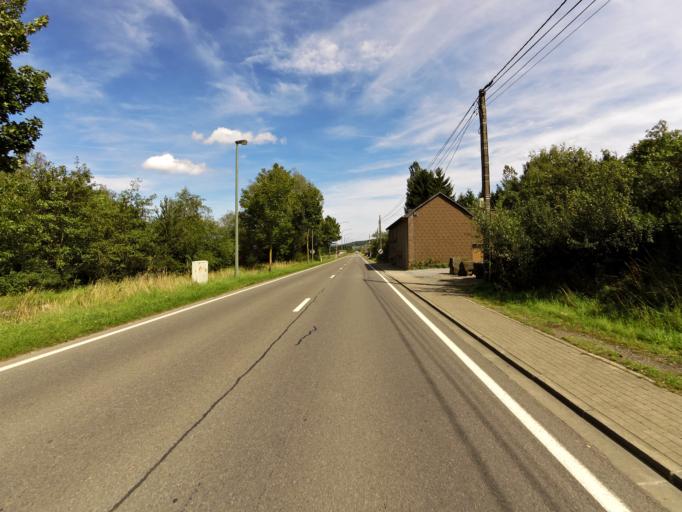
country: BE
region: Wallonia
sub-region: Province du Luxembourg
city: Marche-en-Famenne
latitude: 50.2392
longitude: 5.3716
